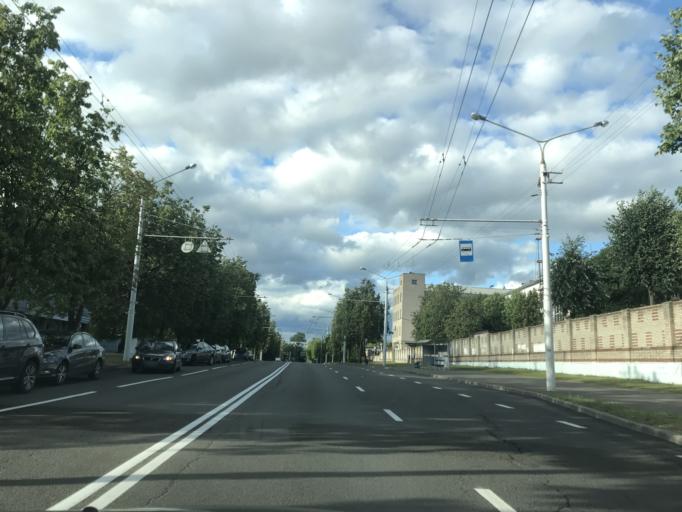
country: BY
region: Minsk
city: Minsk
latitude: 53.9446
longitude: 27.6217
